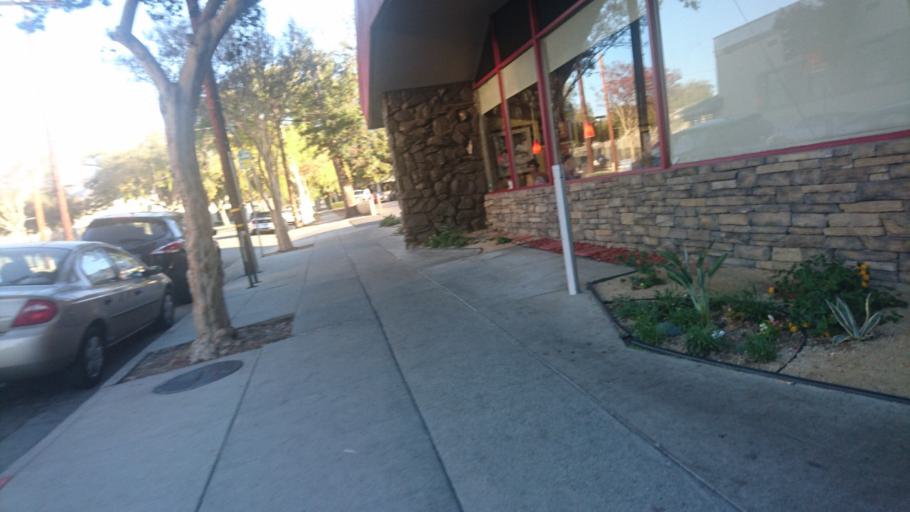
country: US
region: California
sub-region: Los Angeles County
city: East Pasadena
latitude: 34.1463
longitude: -118.0961
